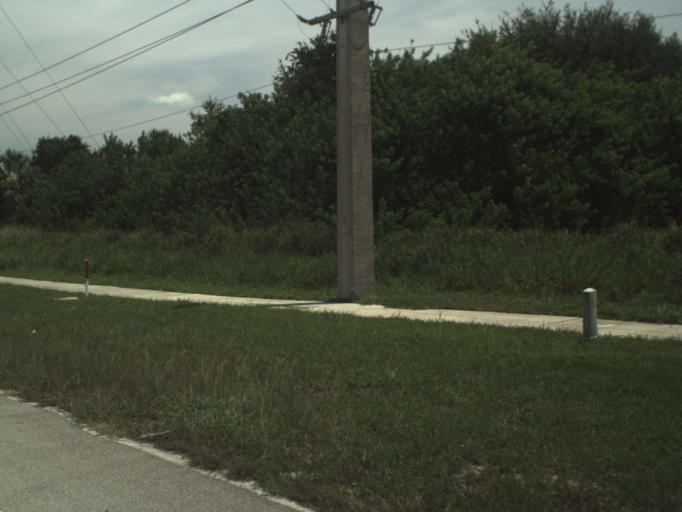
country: US
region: Florida
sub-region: Saint Lucie County
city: Lakewood Park
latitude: 27.5328
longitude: -80.4147
